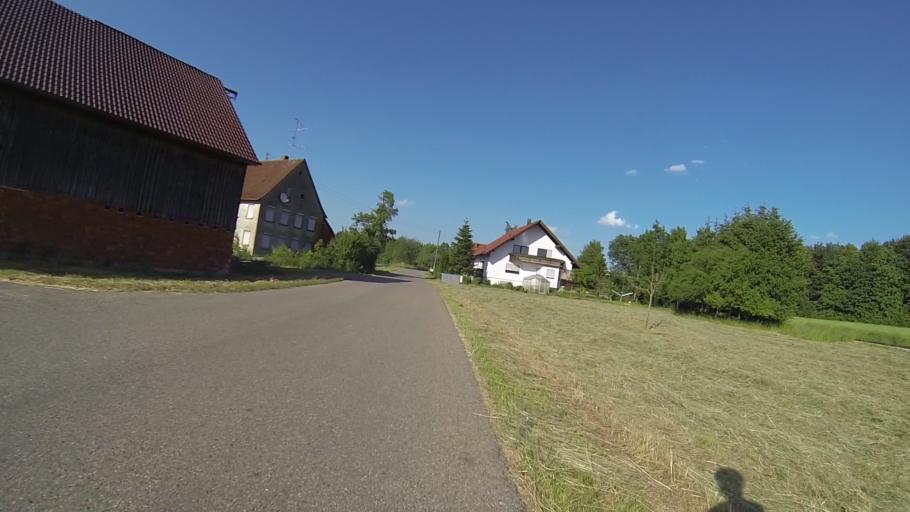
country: DE
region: Baden-Wuerttemberg
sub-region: Tuebingen Region
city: Warthausen
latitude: 48.1458
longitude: 9.8298
